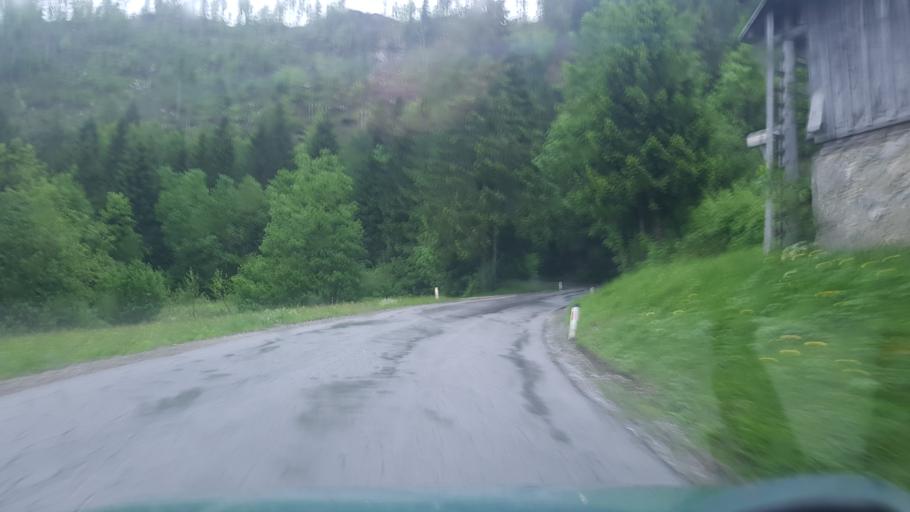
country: SI
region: Bohinj
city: Bohinjska Bistrica
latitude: 46.2695
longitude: 13.9983
